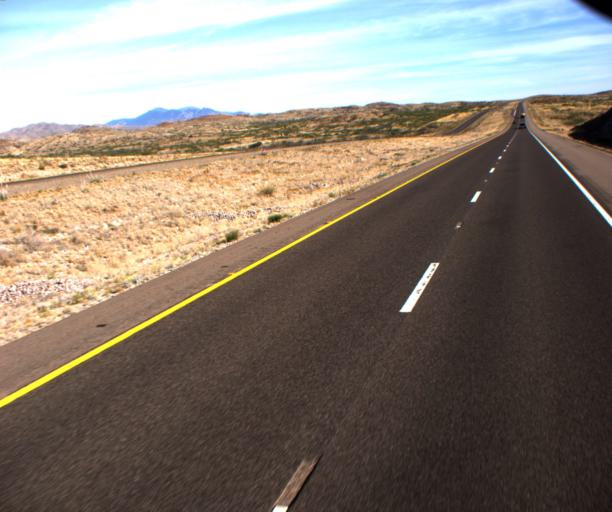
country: US
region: Arizona
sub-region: Cochise County
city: Willcox
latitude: 32.4286
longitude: -109.6629
